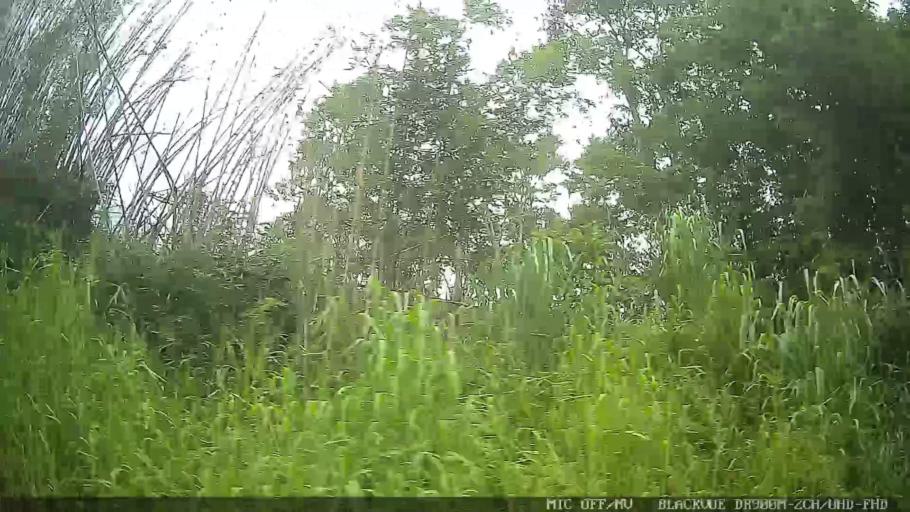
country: BR
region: Sao Paulo
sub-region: Mogi das Cruzes
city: Mogi das Cruzes
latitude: -23.4367
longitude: -46.2296
